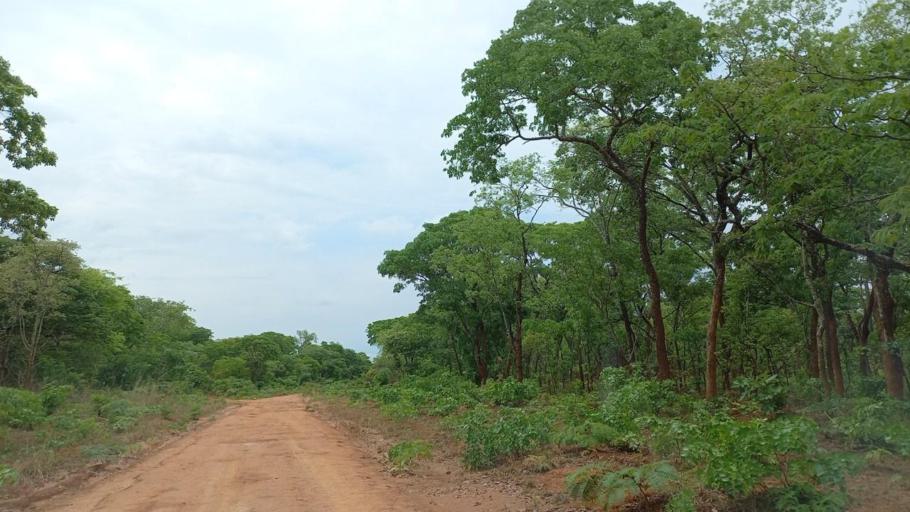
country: ZM
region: North-Western
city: Kalengwa
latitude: -13.6301
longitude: 24.9786
